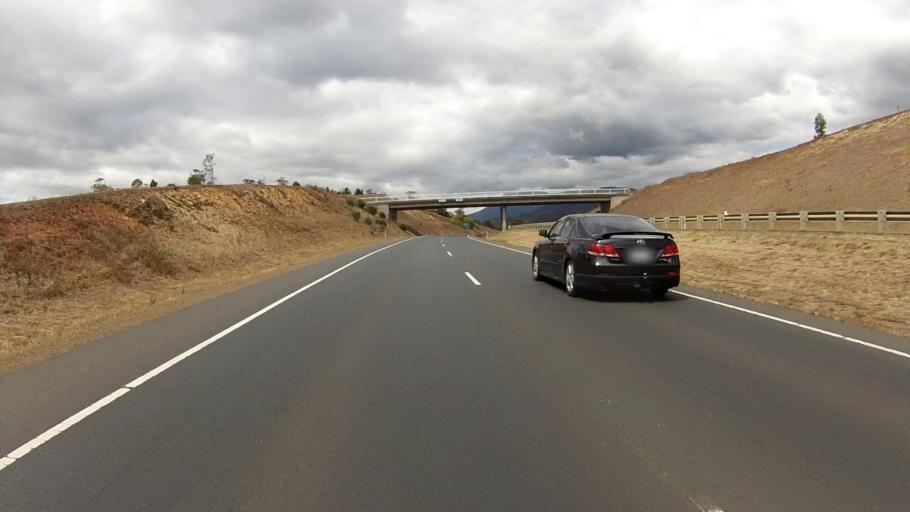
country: AU
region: Tasmania
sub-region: Glenorchy
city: Austins Ferry
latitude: -42.7726
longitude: 147.2389
